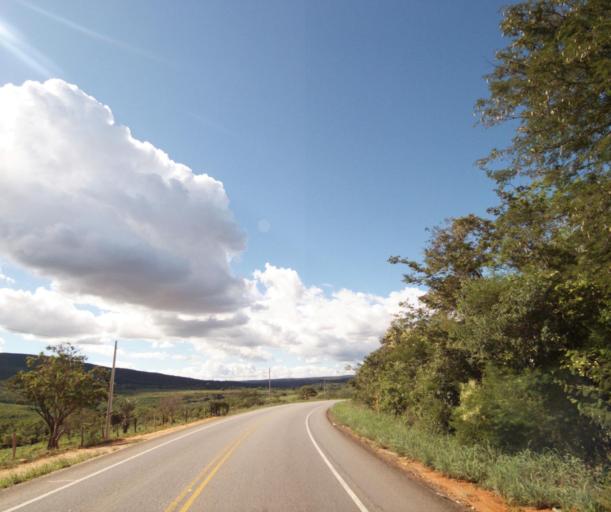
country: BR
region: Bahia
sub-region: Caetite
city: Caetite
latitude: -14.0957
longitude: -42.4475
